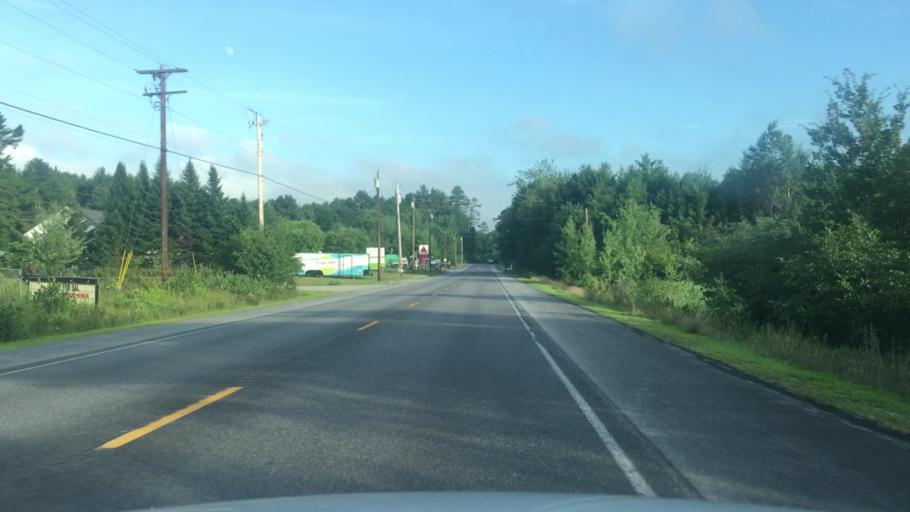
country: US
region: Maine
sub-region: Cumberland County
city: North Windham
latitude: 43.7969
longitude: -70.4011
